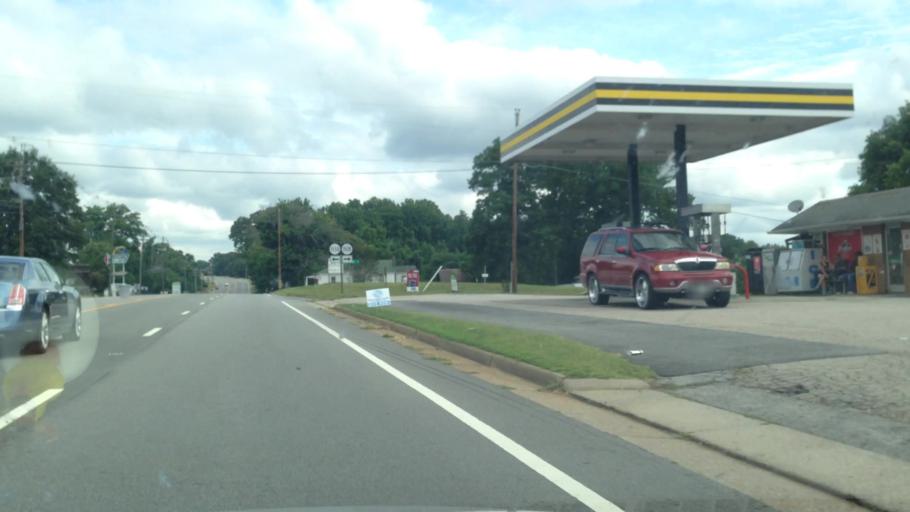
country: US
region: Virginia
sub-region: Pittsylvania County
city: Mount Hermon
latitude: 36.6606
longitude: -79.3755
